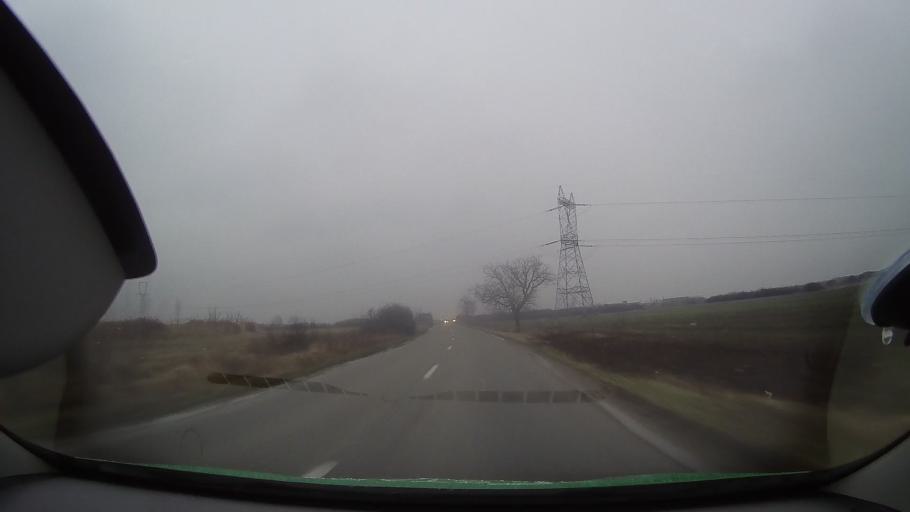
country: RO
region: Bihor
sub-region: Comuna Madaras
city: Madaras
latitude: 46.7933
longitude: 21.6904
